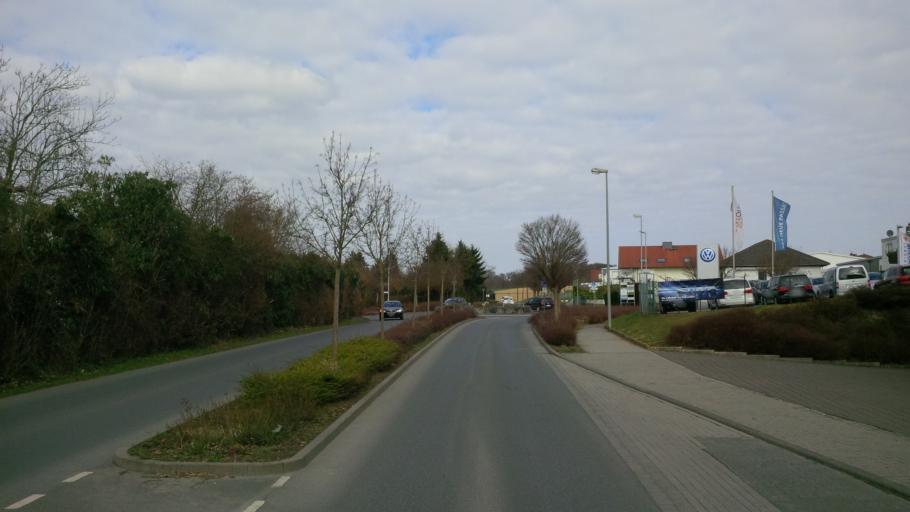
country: DE
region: Hesse
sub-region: Regierungsbezirk Darmstadt
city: Wehrheim
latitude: 50.3087
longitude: 8.5640
